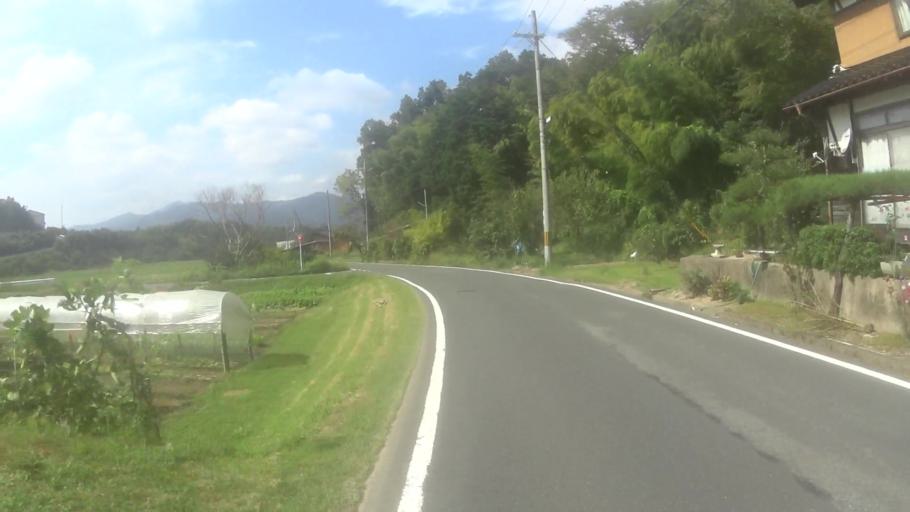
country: JP
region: Kyoto
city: Miyazu
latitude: 35.5879
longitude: 135.1107
